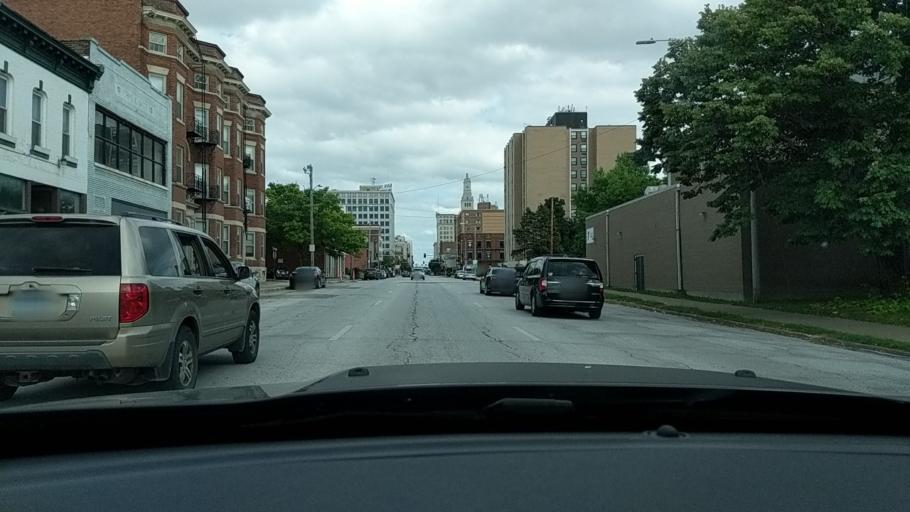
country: US
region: Iowa
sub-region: Scott County
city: Davenport
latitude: 41.5224
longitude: -90.5824
